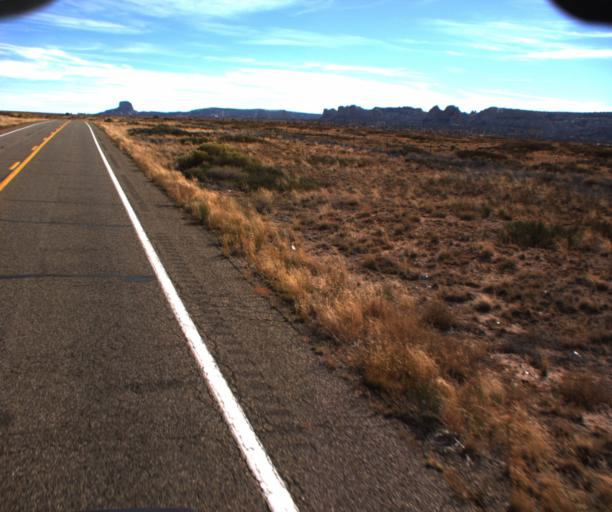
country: US
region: Arizona
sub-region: Coconino County
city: Kaibito
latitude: 36.6120
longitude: -111.0183
